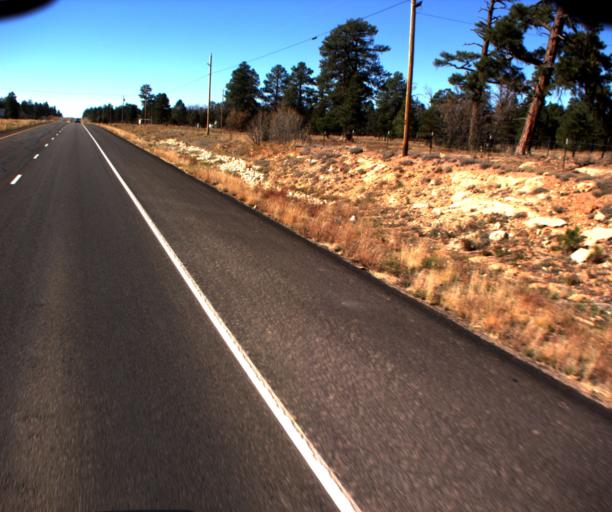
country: US
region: Arizona
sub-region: Apache County
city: Saint Michaels
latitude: 35.6755
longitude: -109.1881
